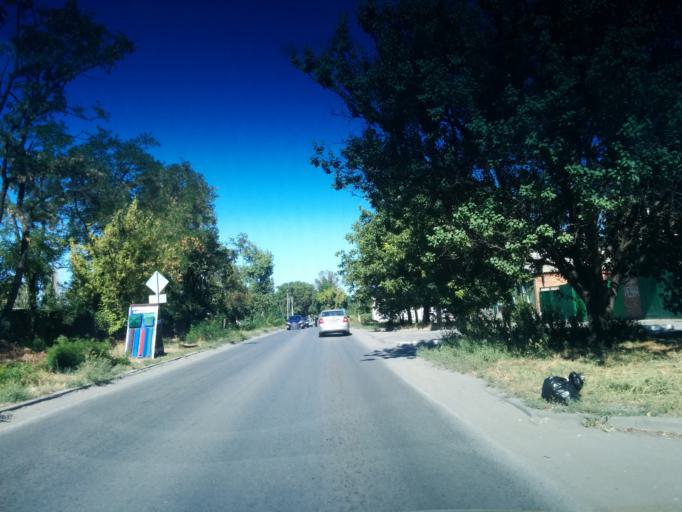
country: RU
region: Rostov
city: Shakhty
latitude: 47.7035
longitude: 40.2276
